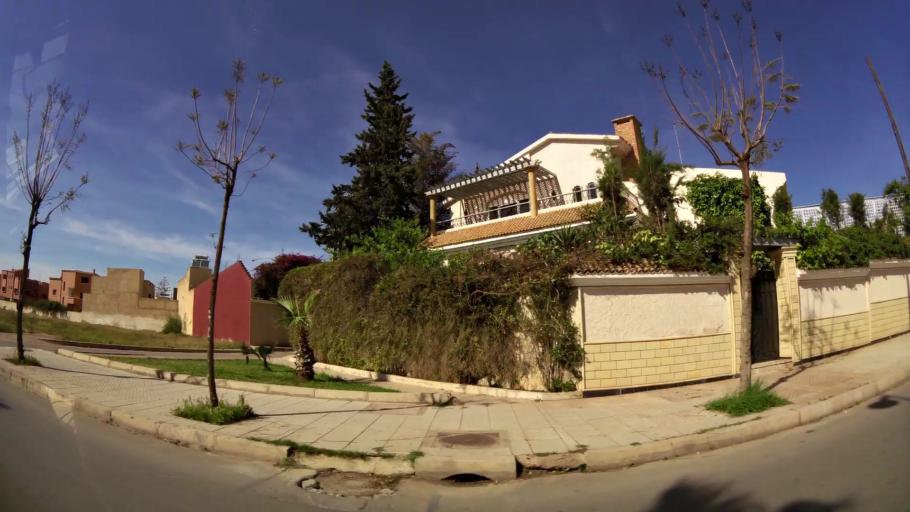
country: MA
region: Oriental
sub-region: Oujda-Angad
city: Oujda
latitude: 34.6688
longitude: -1.9029
